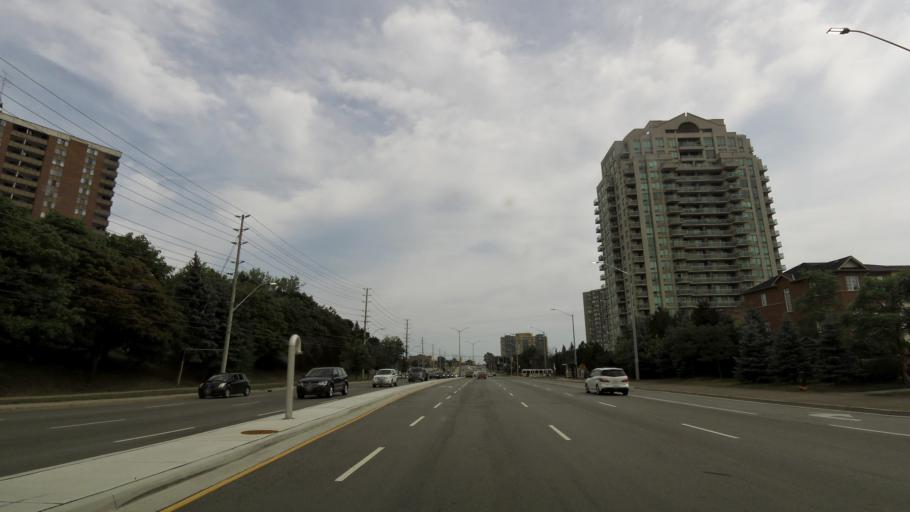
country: CA
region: Ontario
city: Etobicoke
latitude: 43.6272
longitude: -79.6091
